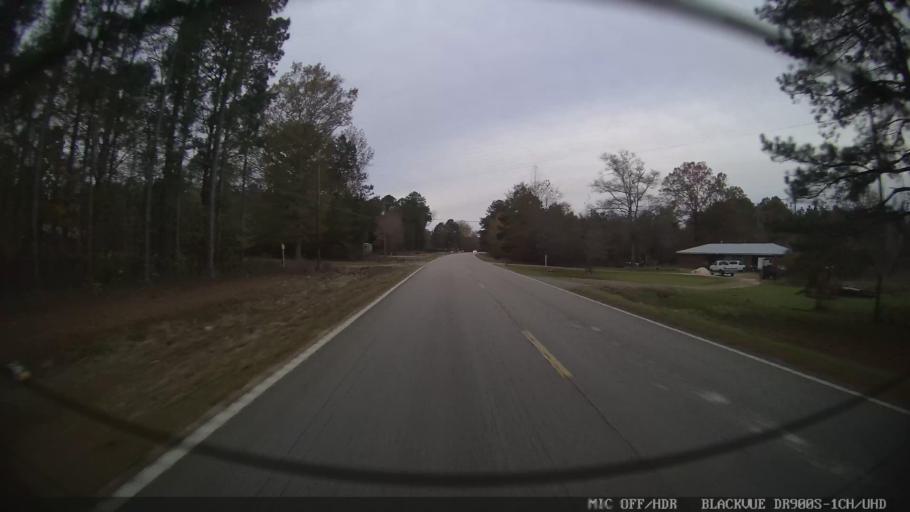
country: US
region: Mississippi
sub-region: Clarke County
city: Stonewall
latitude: 32.0273
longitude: -88.8611
